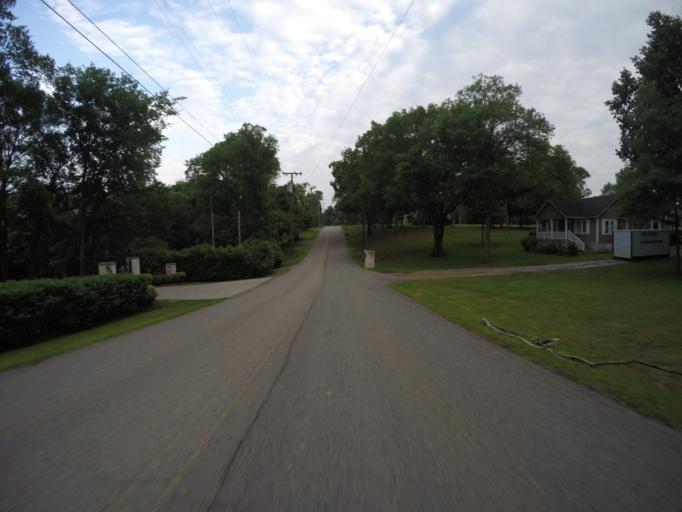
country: US
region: Tennessee
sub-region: Davidson County
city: Lakewood
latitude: 36.2427
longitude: -86.6258
